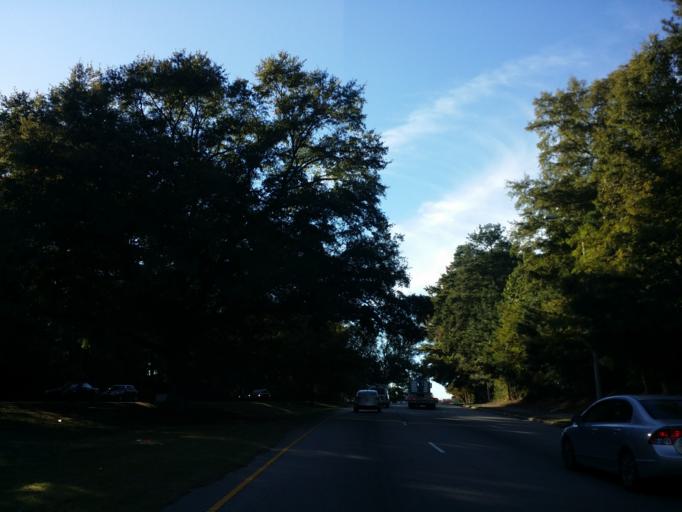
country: US
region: North Carolina
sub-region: Wake County
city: West Raleigh
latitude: 35.7797
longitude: -78.6708
